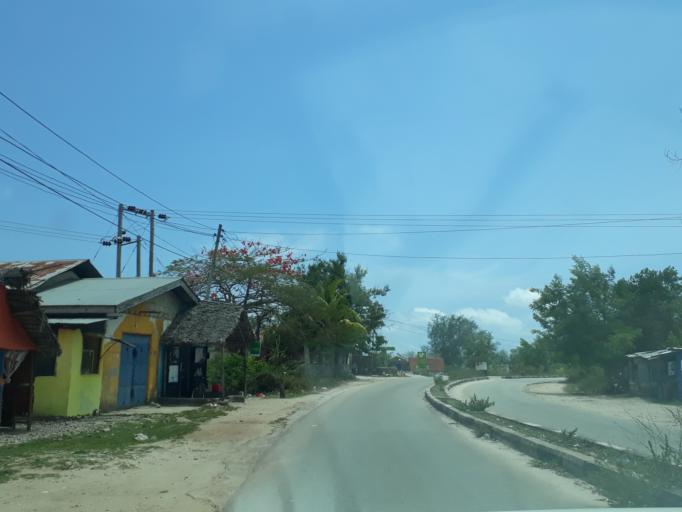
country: TZ
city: Kiwengwa
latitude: -5.9902
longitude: 39.3750
